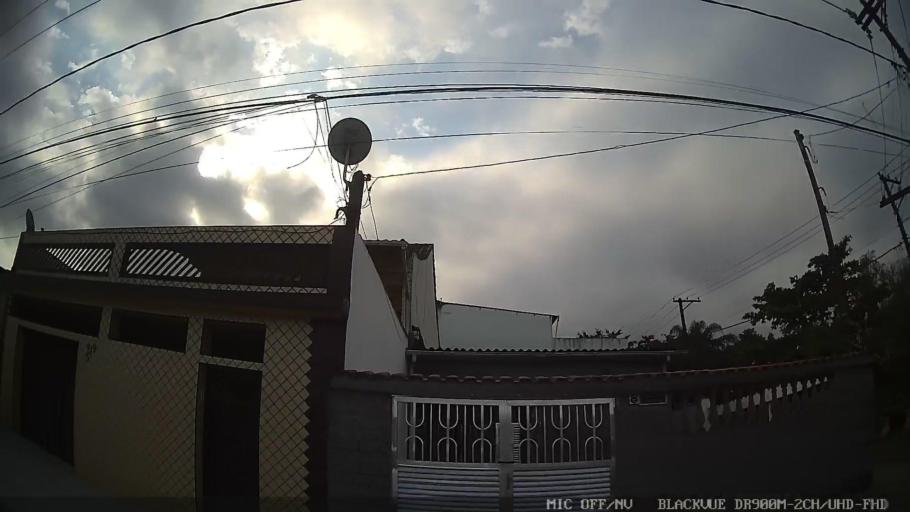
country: BR
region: Sao Paulo
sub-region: Guaruja
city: Guaruja
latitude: -23.9548
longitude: -46.2763
